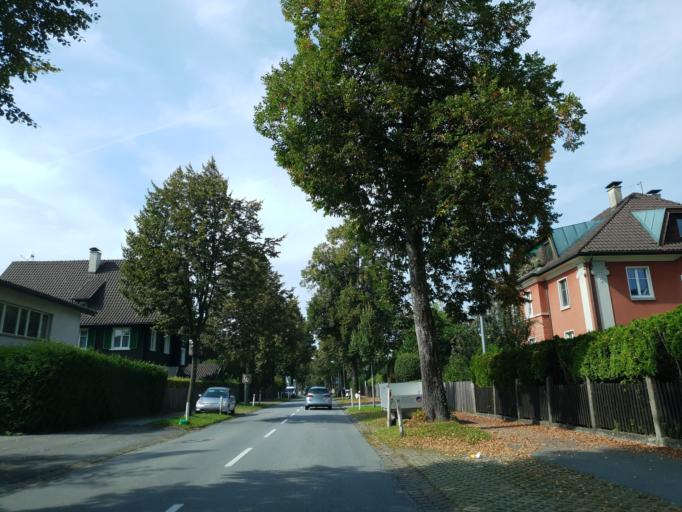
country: AT
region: Vorarlberg
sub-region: Politischer Bezirk Bregenz
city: Bregenz
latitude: 47.4953
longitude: 9.7379
